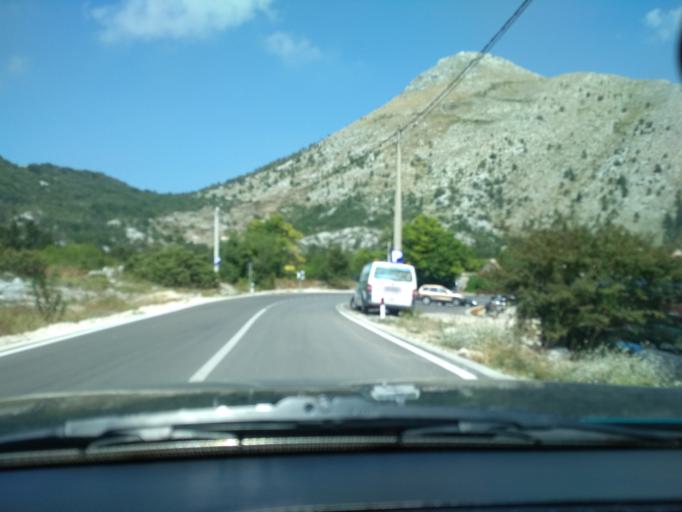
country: ME
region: Kotor
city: Kotor
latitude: 42.4265
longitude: 18.8002
